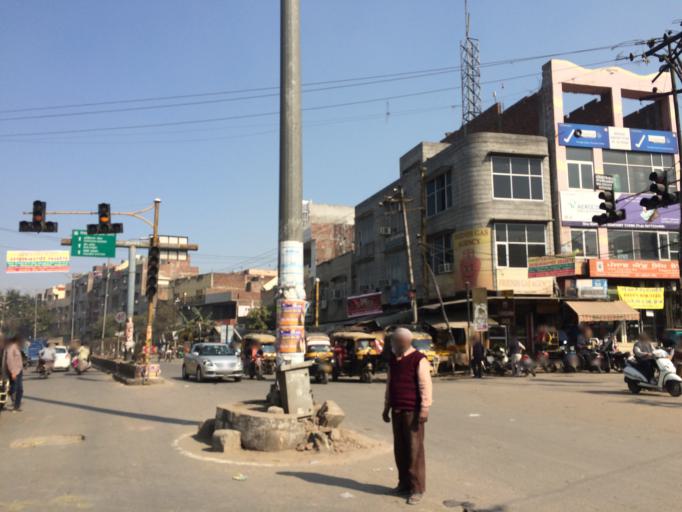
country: IN
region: Punjab
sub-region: Amritsar
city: Amritsar
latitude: 31.6247
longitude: 74.8689
